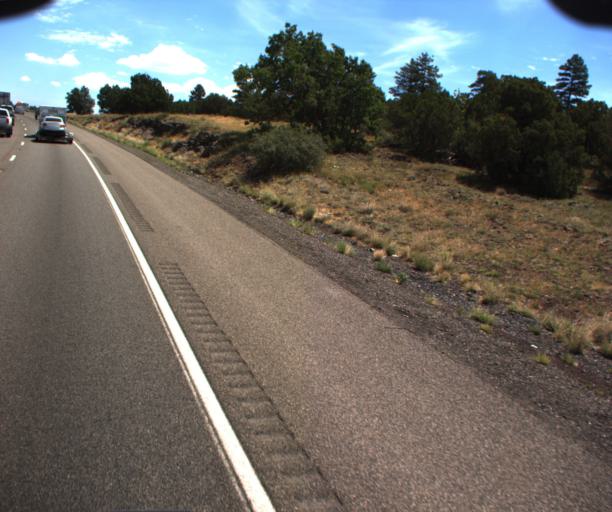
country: US
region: Arizona
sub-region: Yavapai County
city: Village of Oak Creek (Big Park)
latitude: 34.7867
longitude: -111.5946
